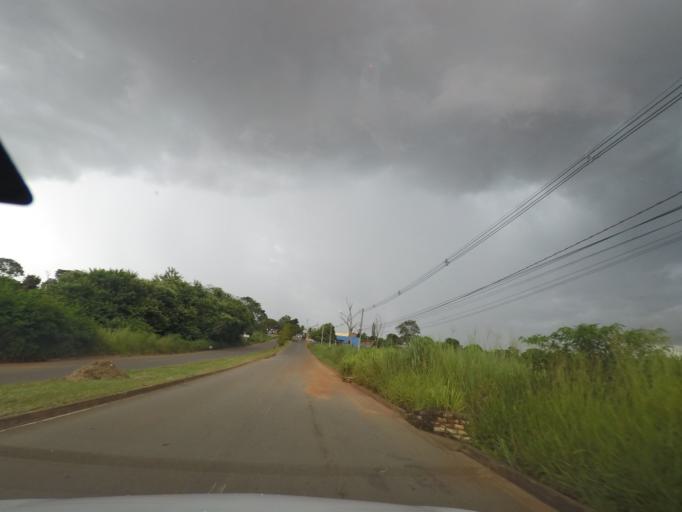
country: BR
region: Goias
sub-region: Goiania
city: Goiania
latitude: -16.7302
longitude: -49.3681
